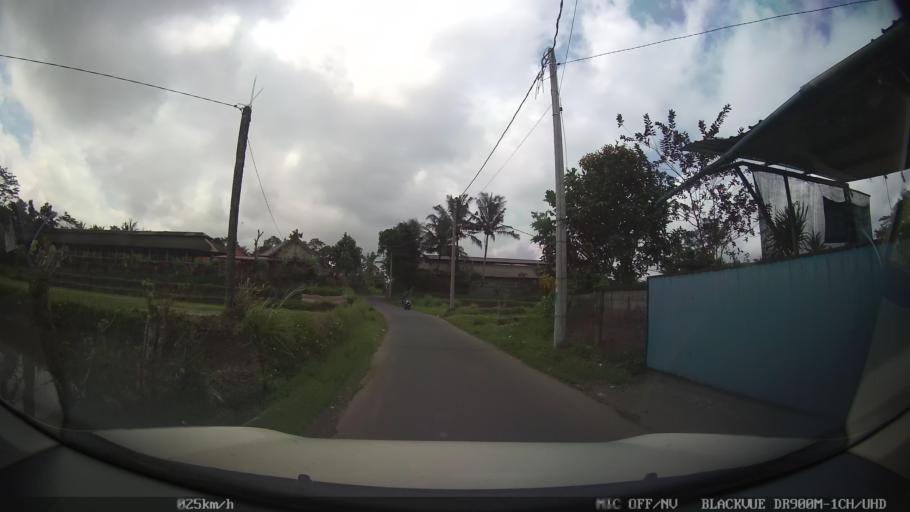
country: ID
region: Bali
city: Banjar Petak
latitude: -8.4429
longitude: 115.3225
